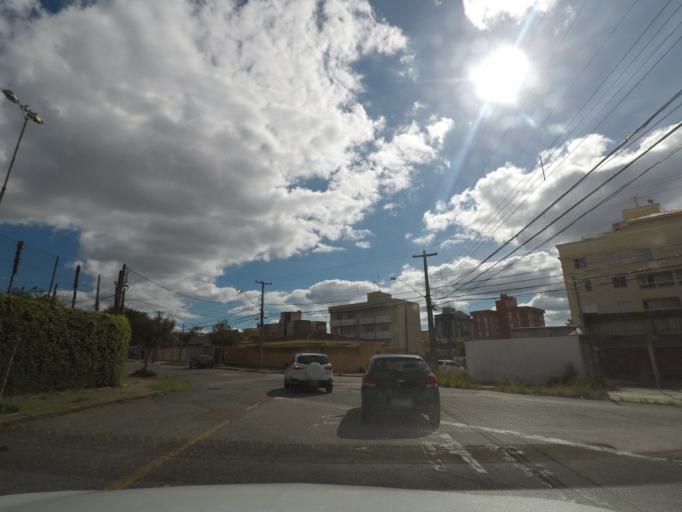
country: BR
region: Parana
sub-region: Curitiba
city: Curitiba
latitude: -25.4387
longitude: -49.2446
